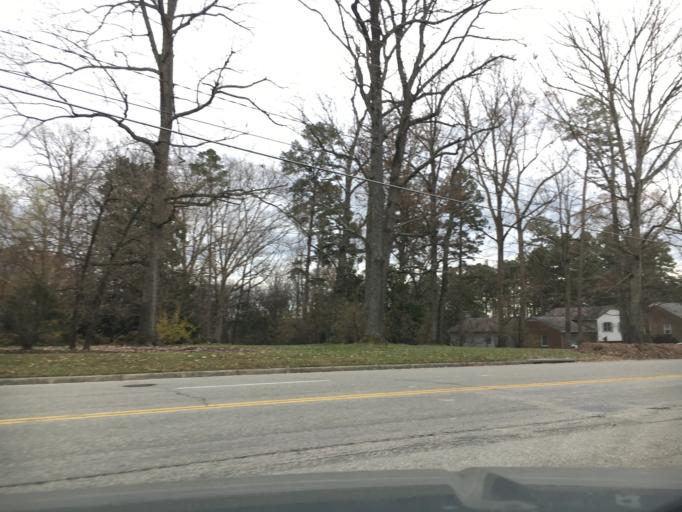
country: US
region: Virginia
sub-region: Halifax County
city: South Boston
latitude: 36.7303
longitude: -78.9060
